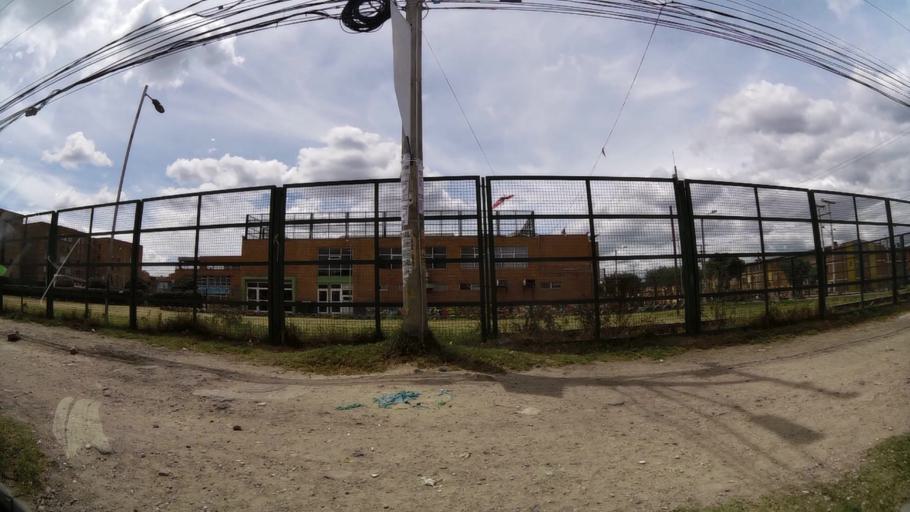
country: CO
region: Cundinamarca
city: Soacha
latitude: 4.6422
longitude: -74.1639
